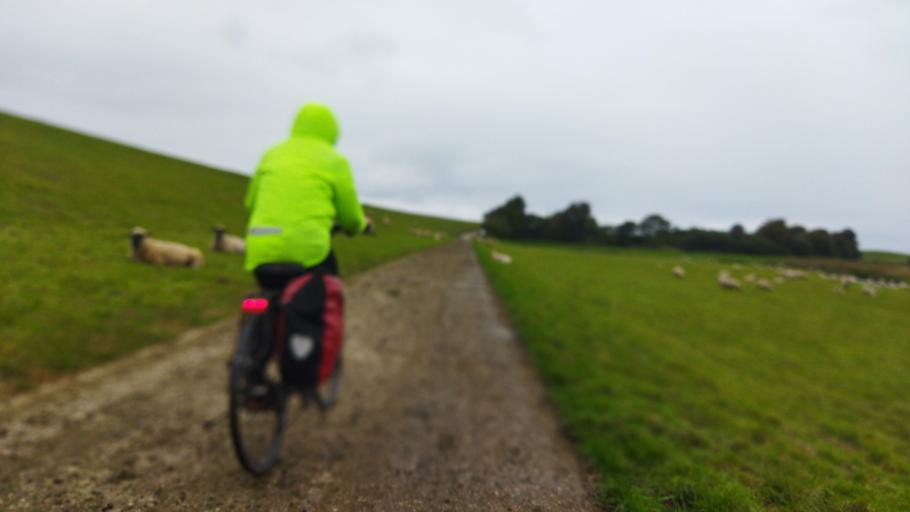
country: DE
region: Lower Saxony
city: Hinte
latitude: 53.4813
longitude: 7.0295
